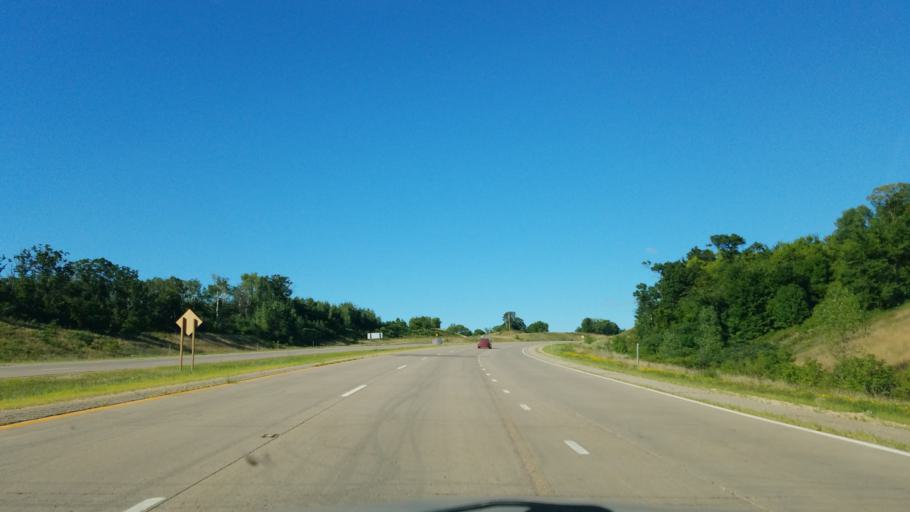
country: US
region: Wisconsin
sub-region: Saint Croix County
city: Somerset
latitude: 45.1034
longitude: -92.7300
